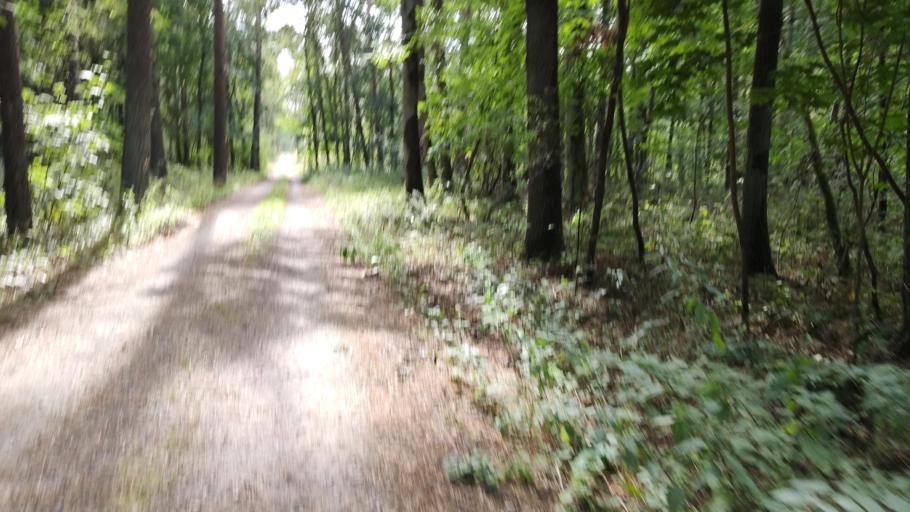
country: PL
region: Kujawsko-Pomorskie
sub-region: Powiat zninski
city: Barcin
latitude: 52.8311
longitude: 17.9422
